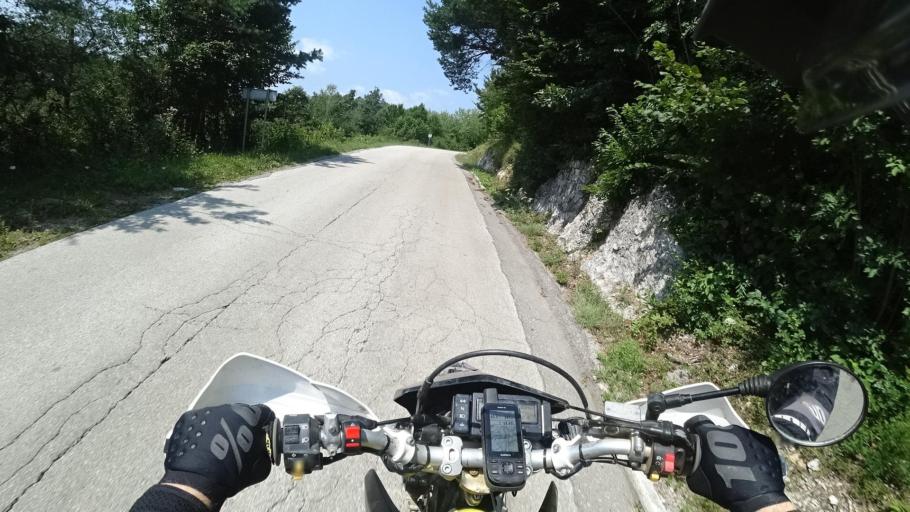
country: HR
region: Karlovacka
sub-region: Grad Ogulin
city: Ogulin
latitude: 45.3139
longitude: 15.1746
